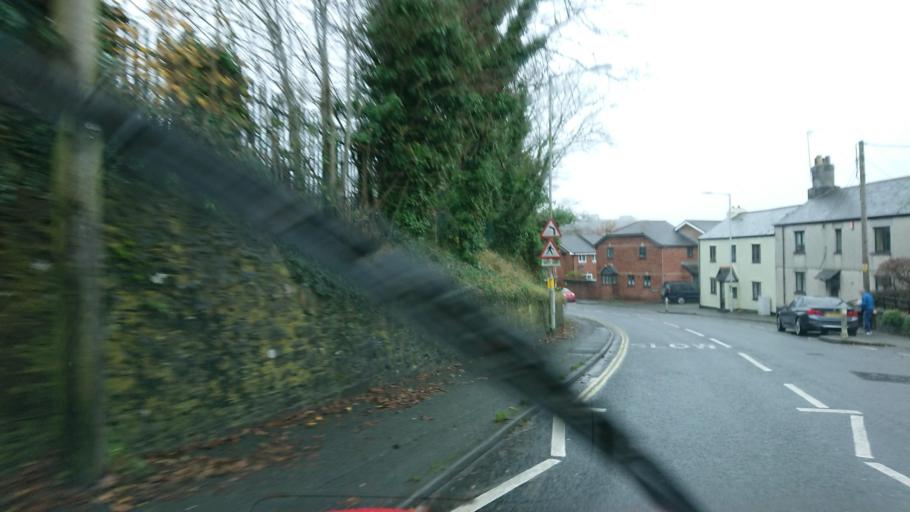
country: GB
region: England
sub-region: Plymouth
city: Plymstock
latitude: 50.3530
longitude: -4.1109
